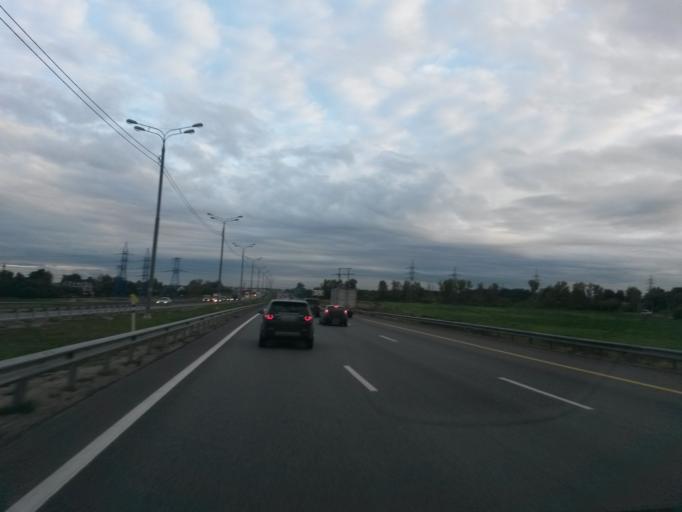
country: RU
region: Moskovskaya
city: Yam
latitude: 55.4924
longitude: 37.7347
